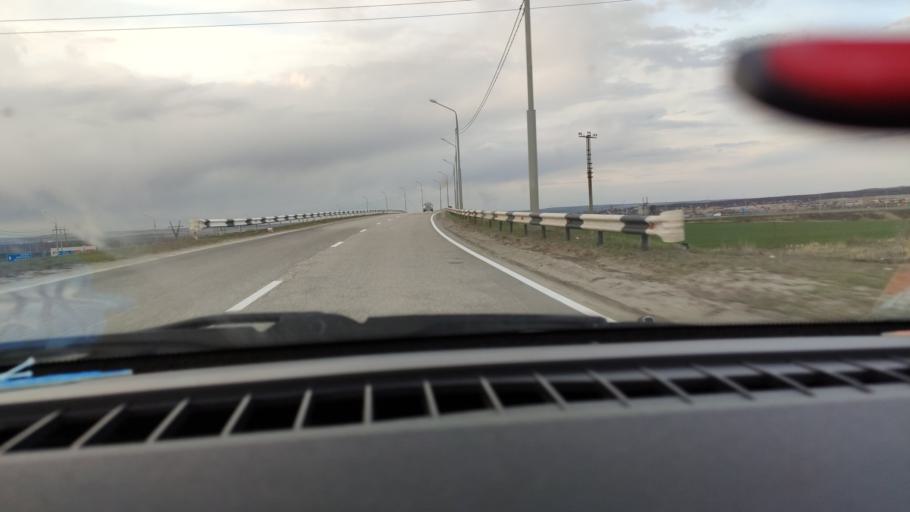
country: RU
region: Saratov
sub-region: Saratovskiy Rayon
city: Saratov
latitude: 51.6708
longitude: 46.0009
